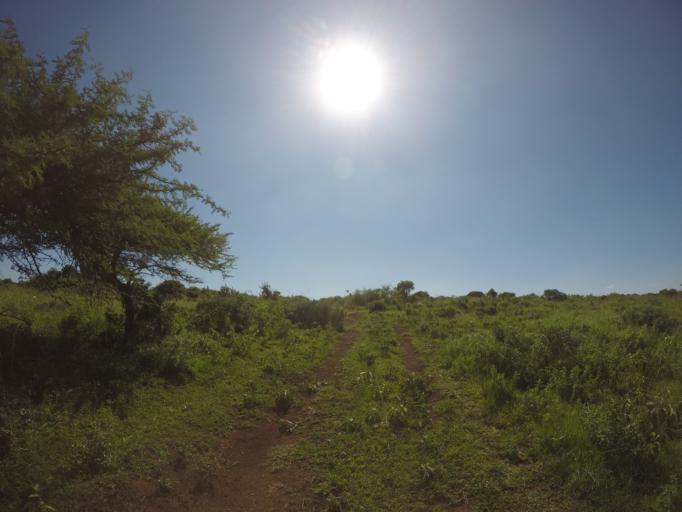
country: ZA
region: KwaZulu-Natal
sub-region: uThungulu District Municipality
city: Empangeni
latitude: -28.5705
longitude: 31.7016
